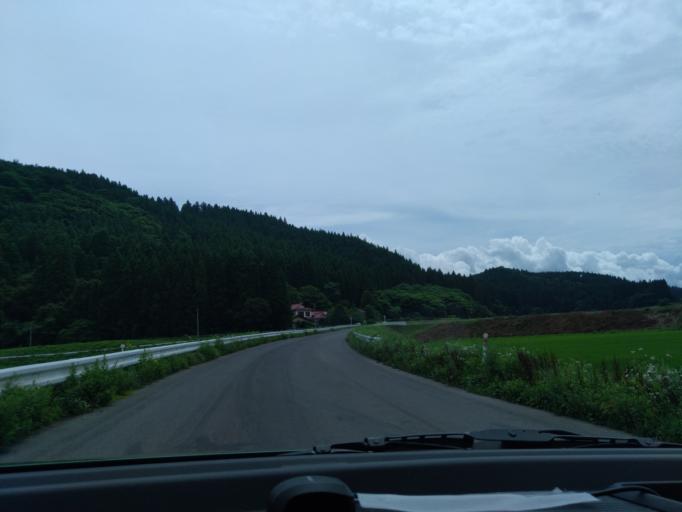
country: JP
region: Akita
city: Kakunodatemachi
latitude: 39.5952
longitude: 140.6175
